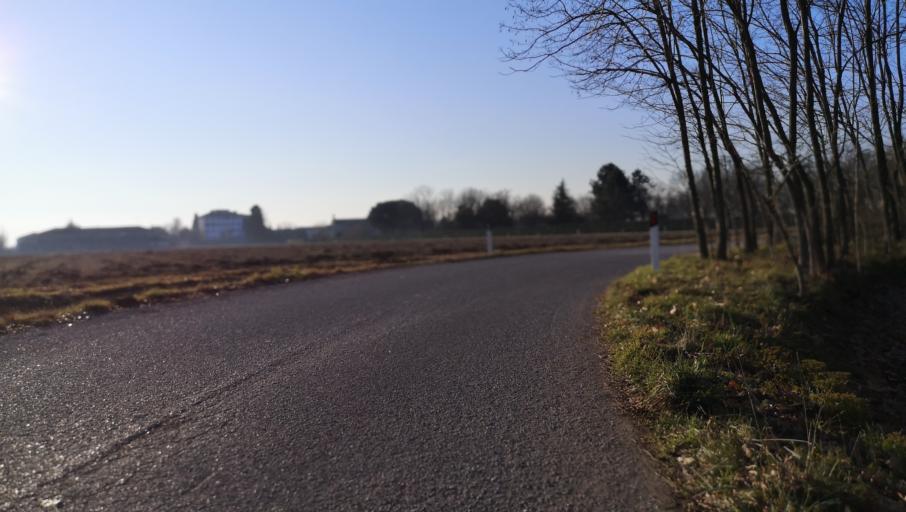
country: IT
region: Friuli Venezia Giulia
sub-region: Provincia di Udine
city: Pavia di Udine
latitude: 45.9867
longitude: 13.3020
